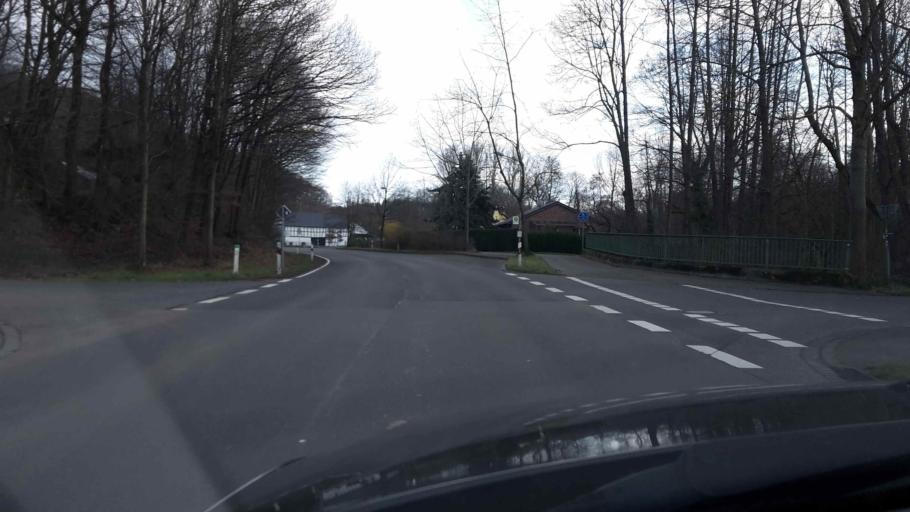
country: DE
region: North Rhine-Westphalia
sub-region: Regierungsbezirk Koln
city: Bad Honnef
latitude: 50.6940
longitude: 7.2922
